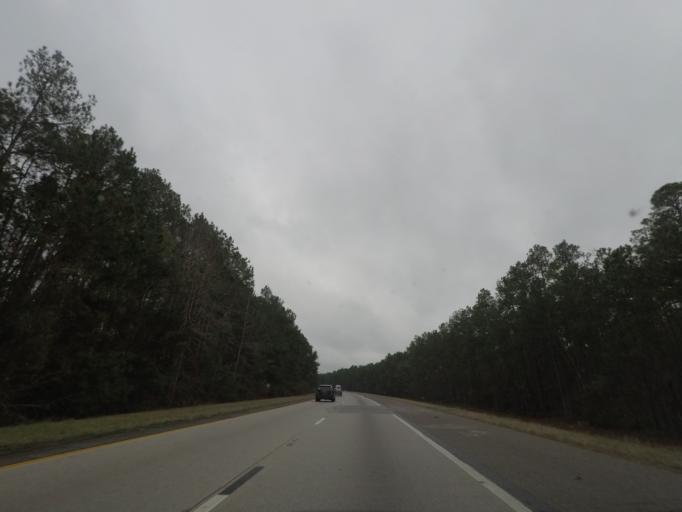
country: US
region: South Carolina
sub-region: Colleton County
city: Walterboro
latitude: 33.0443
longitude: -80.6700
